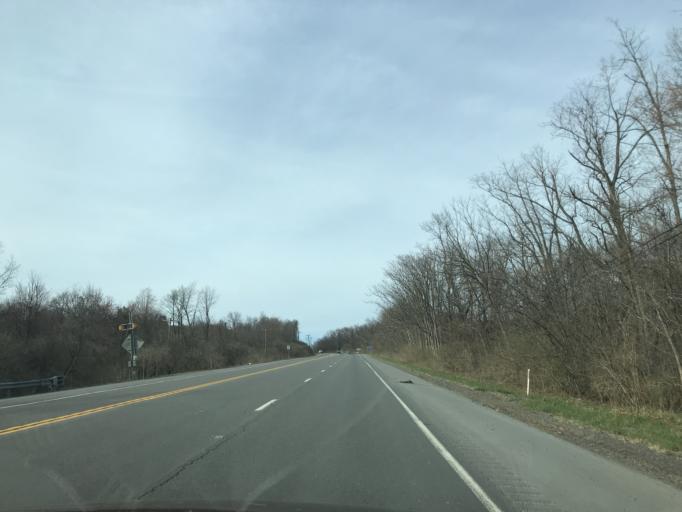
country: US
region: Pennsylvania
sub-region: Lycoming County
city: Montgomery
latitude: 41.1533
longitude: -76.9093
